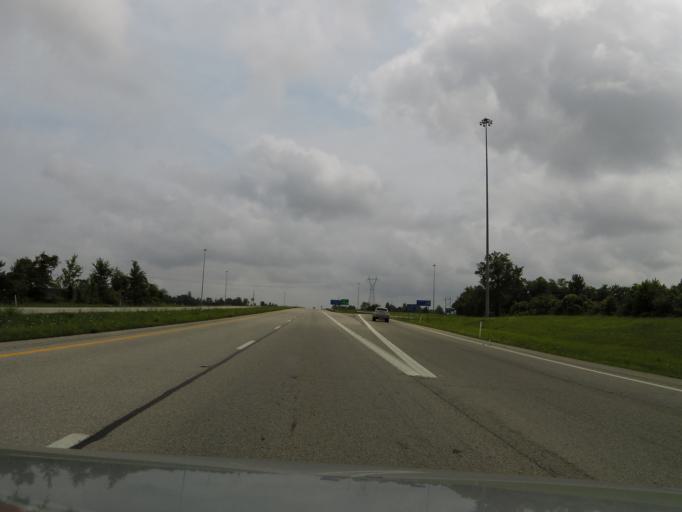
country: US
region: Kentucky
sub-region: Ohio County
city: Beaver Dam
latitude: 37.3653
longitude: -86.8466
